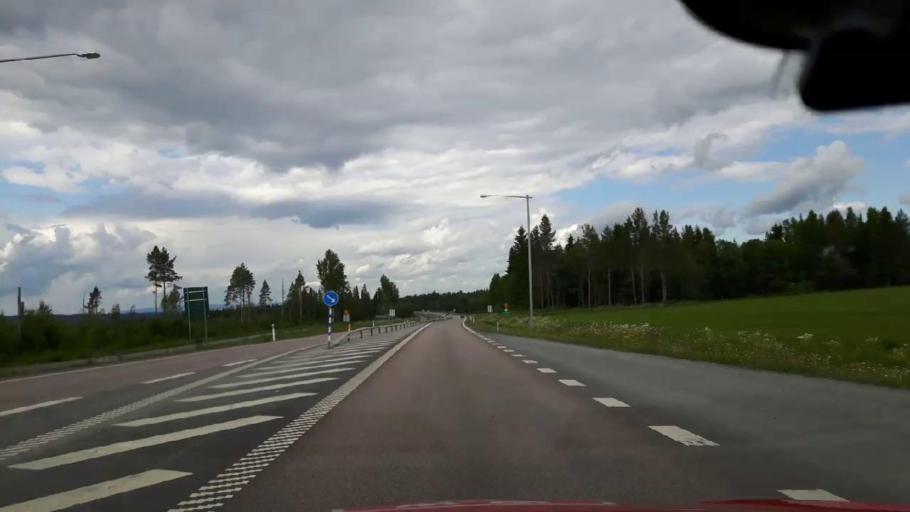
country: SE
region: Jaemtland
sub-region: Krokoms Kommun
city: Krokom
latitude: 63.2687
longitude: 14.5385
